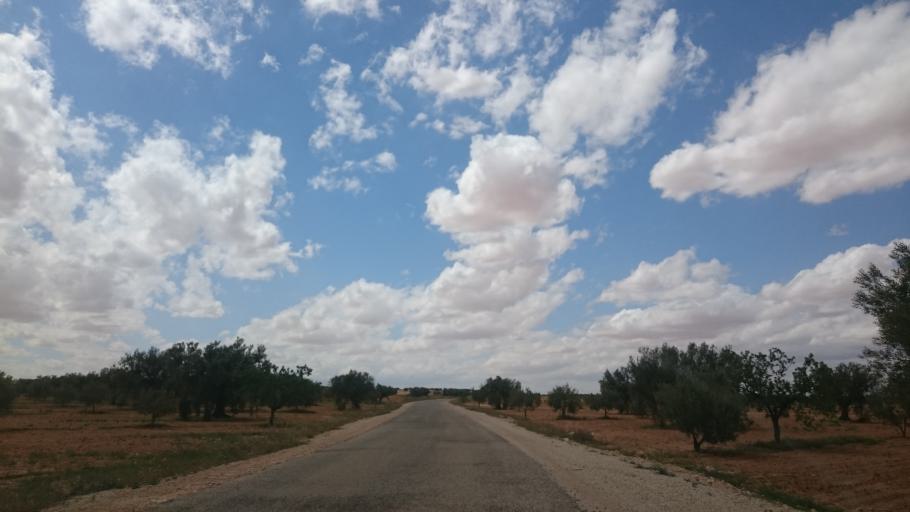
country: TN
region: Safaqis
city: Bi'r `Ali Bin Khalifah
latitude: 34.7776
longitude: 10.3595
